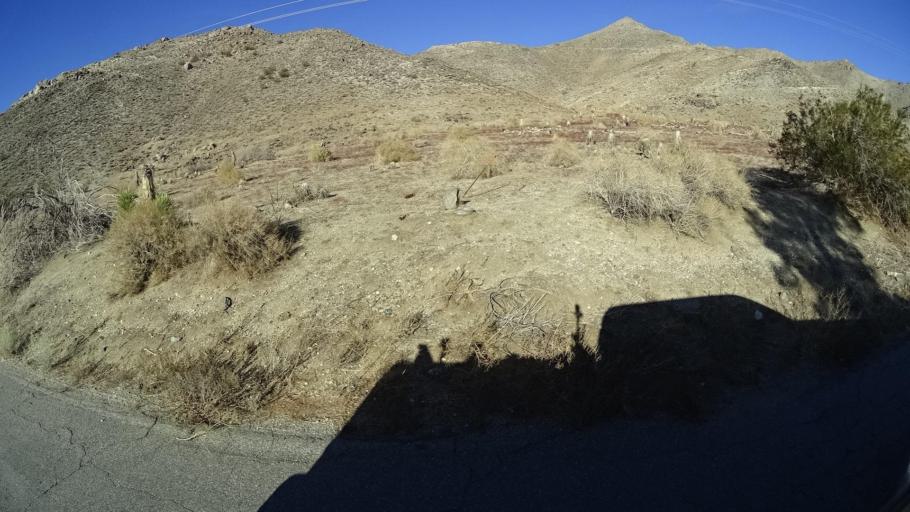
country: US
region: California
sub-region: Kern County
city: Weldon
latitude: 35.5646
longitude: -118.2433
